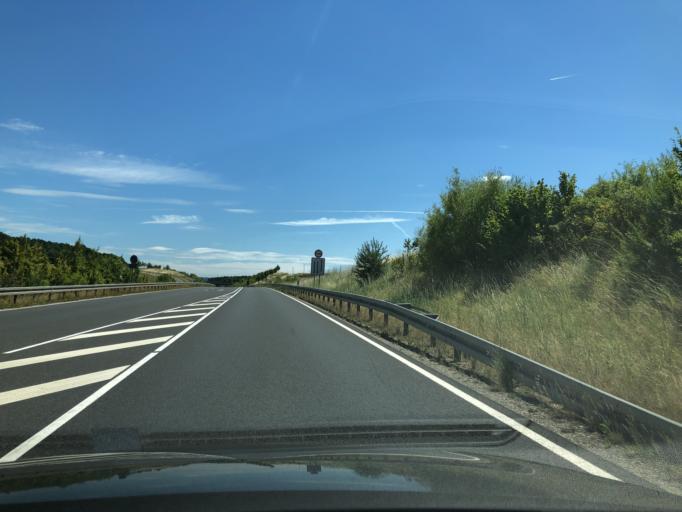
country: DE
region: Bavaria
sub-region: Upper Franconia
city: Untersiemau
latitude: 50.1722
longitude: 10.9897
